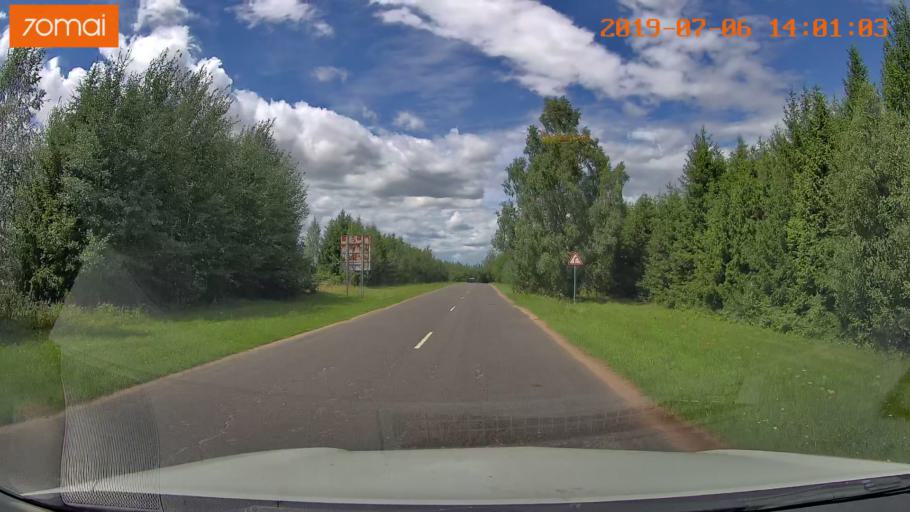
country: BY
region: Minsk
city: Ivyanyets
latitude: 53.8042
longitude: 26.8165
